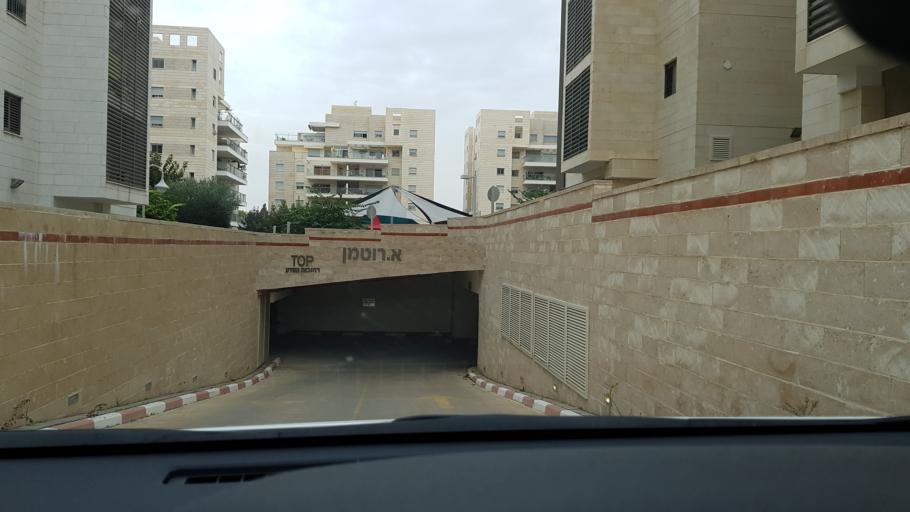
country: IL
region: Central District
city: Ness Ziona
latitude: 31.9035
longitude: 34.8196
